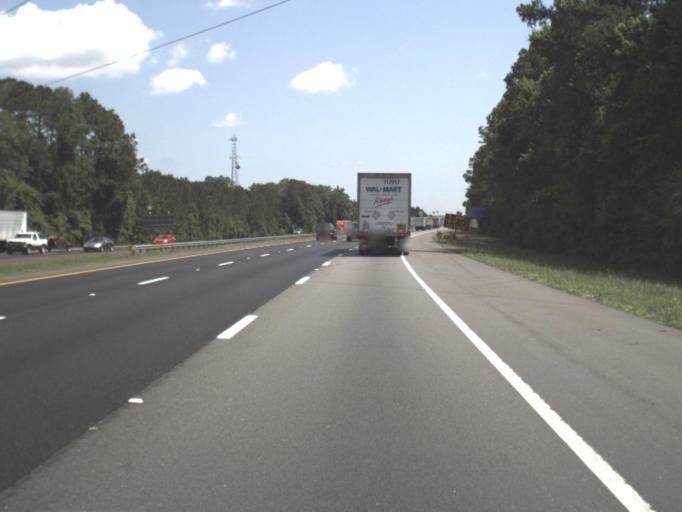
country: US
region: Georgia
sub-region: Camden County
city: Kingsland
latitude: 30.7035
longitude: -81.6753
